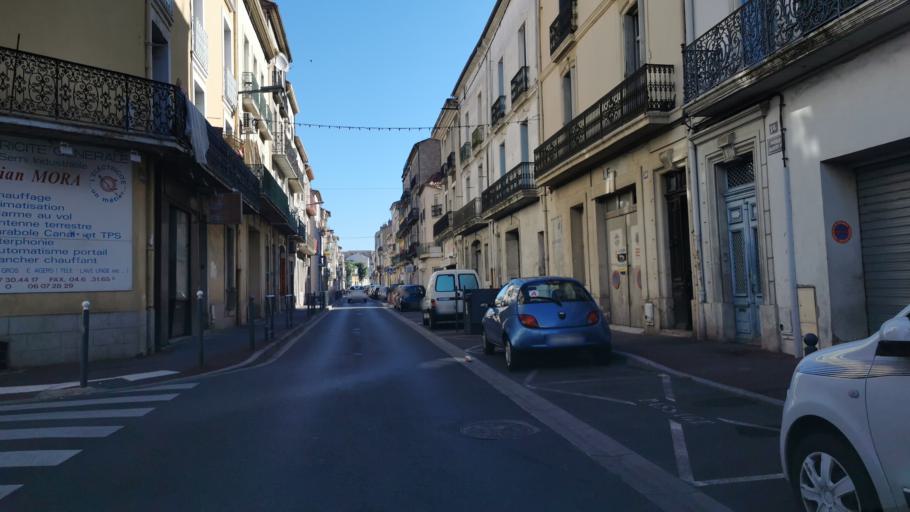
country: FR
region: Languedoc-Roussillon
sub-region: Departement de l'Herault
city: Beziers
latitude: 43.3487
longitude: 3.2175
